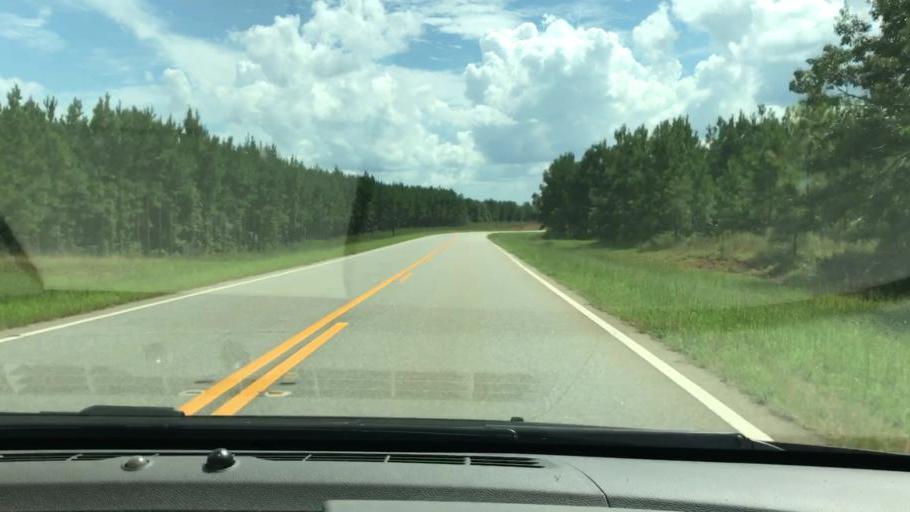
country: US
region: Georgia
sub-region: Quitman County
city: Georgetown
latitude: 31.9170
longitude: -85.0592
